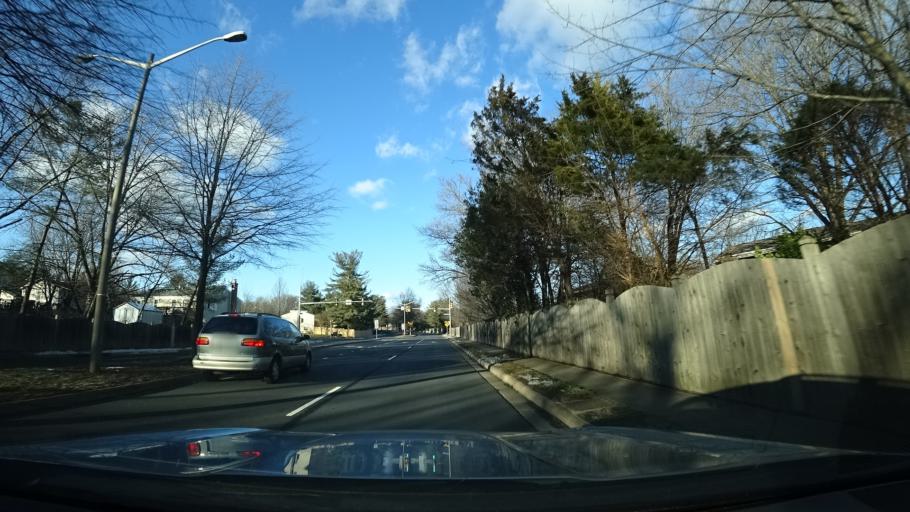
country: US
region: Virginia
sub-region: Fairfax County
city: Herndon
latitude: 38.9773
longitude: -77.3709
